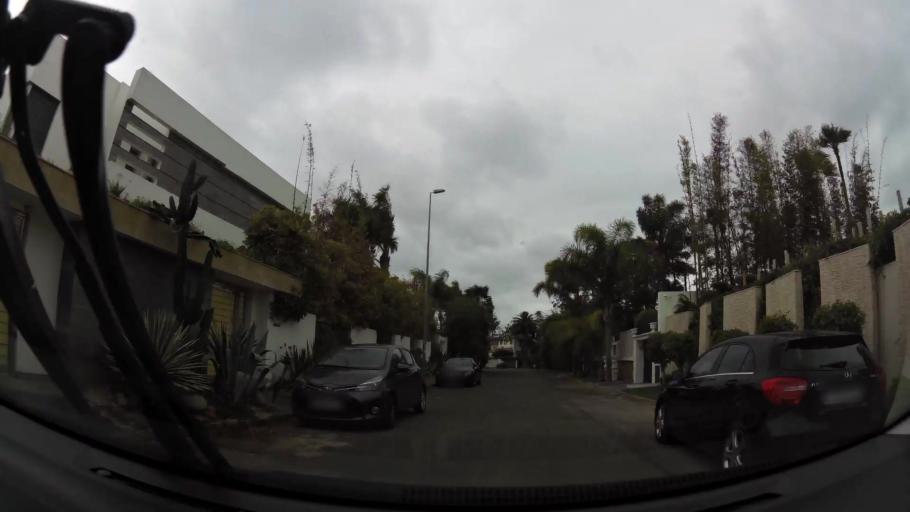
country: MA
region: Grand Casablanca
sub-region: Casablanca
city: Casablanca
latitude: 33.5950
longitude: -7.6651
